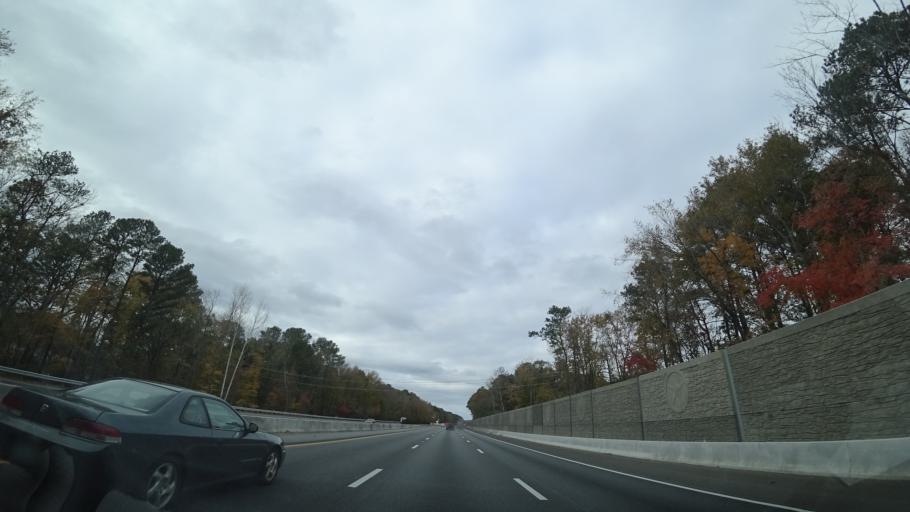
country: US
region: Virginia
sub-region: York County
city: Yorktown
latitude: 37.1403
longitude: -76.5297
